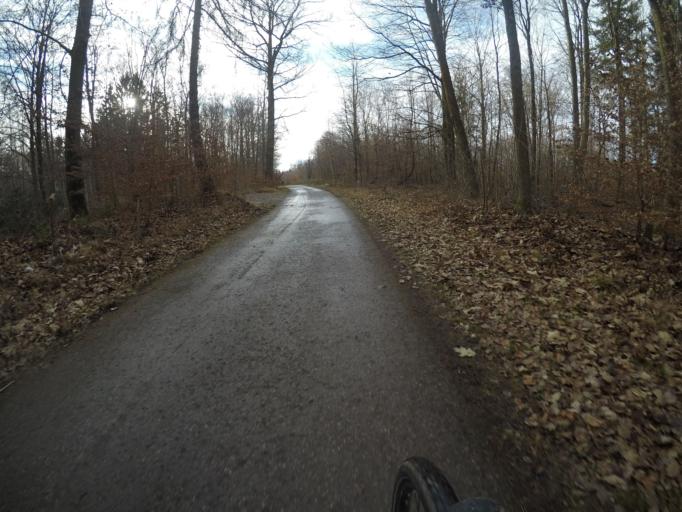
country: DE
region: Baden-Wuerttemberg
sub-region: Regierungsbezirk Stuttgart
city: Sindelfingen
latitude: 48.7151
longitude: 9.0429
